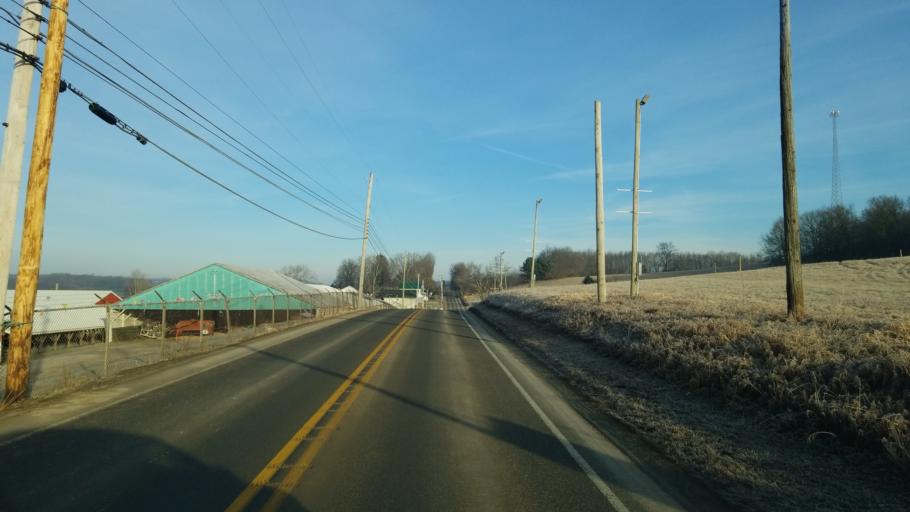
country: US
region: Pennsylvania
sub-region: Indiana County
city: Chevy Chase Heights
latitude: 40.8743
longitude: -79.2392
